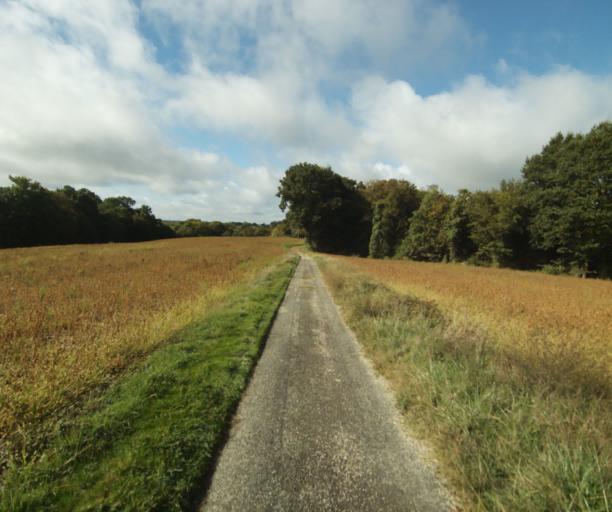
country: FR
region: Midi-Pyrenees
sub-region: Departement du Gers
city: Nogaro
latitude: 43.8375
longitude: -0.0541
